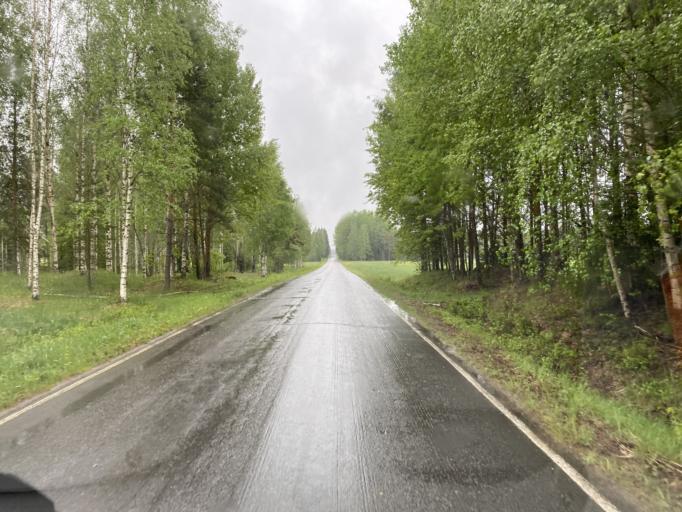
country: FI
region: Haeme
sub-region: Forssa
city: Humppila
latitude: 61.0642
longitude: 23.3238
